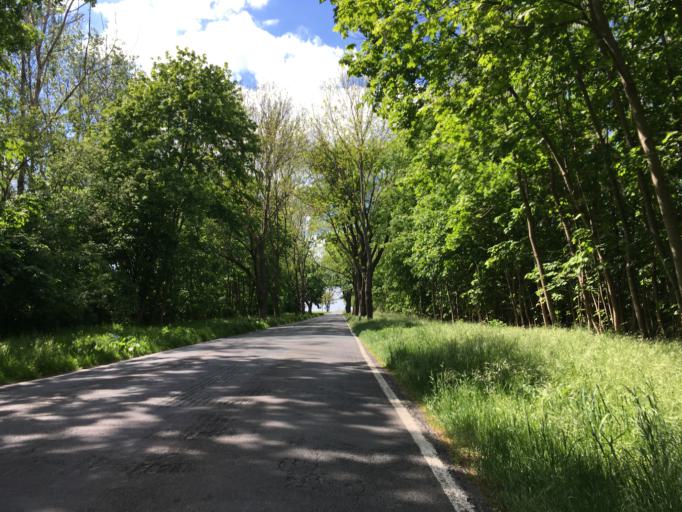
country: DE
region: Brandenburg
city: Rudnitz
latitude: 52.6662
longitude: 13.6601
